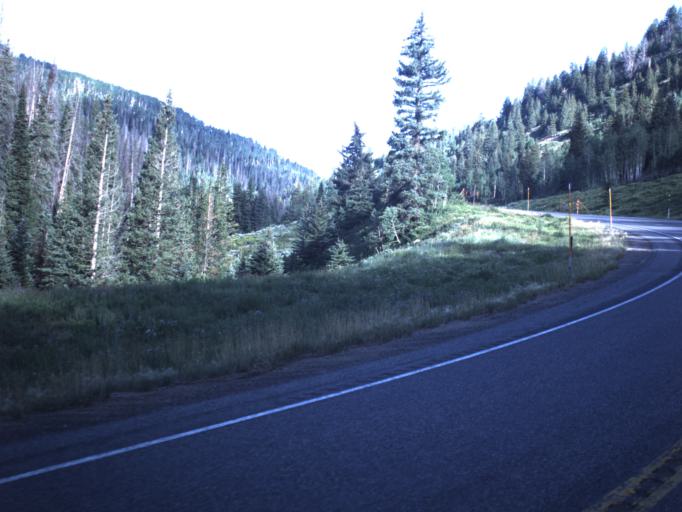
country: US
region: Utah
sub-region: Sanpete County
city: Fairview
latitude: 39.5895
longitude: -111.1942
